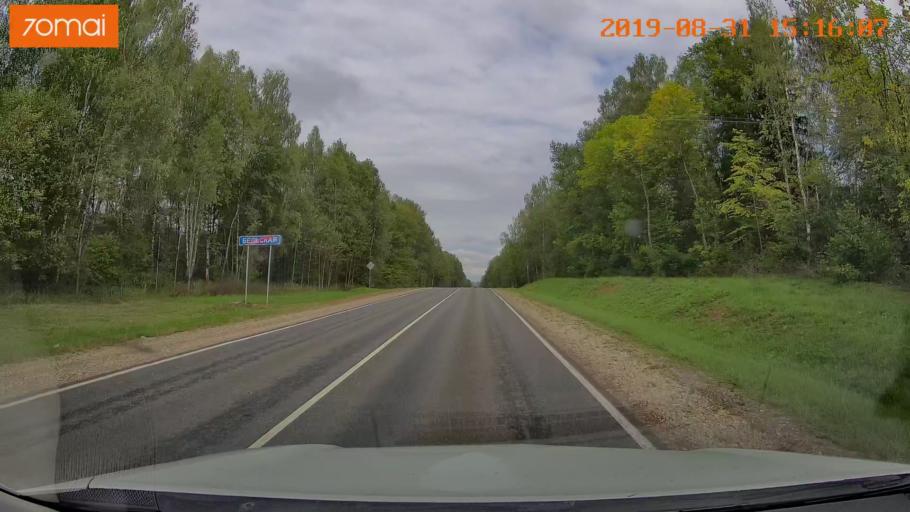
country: RU
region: Kaluga
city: Baryatino
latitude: 54.4572
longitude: 34.3426
